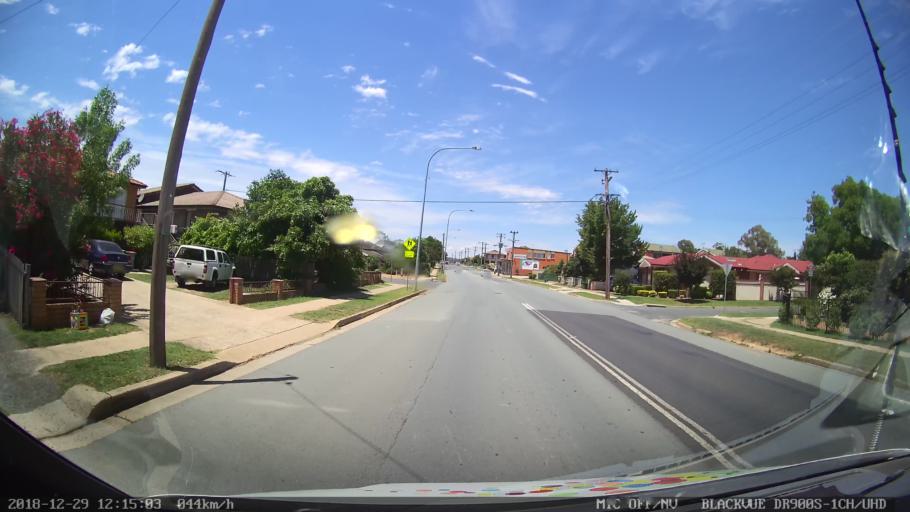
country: AU
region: New South Wales
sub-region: Queanbeyan
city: Queanbeyan
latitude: -35.3592
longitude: 149.2332
